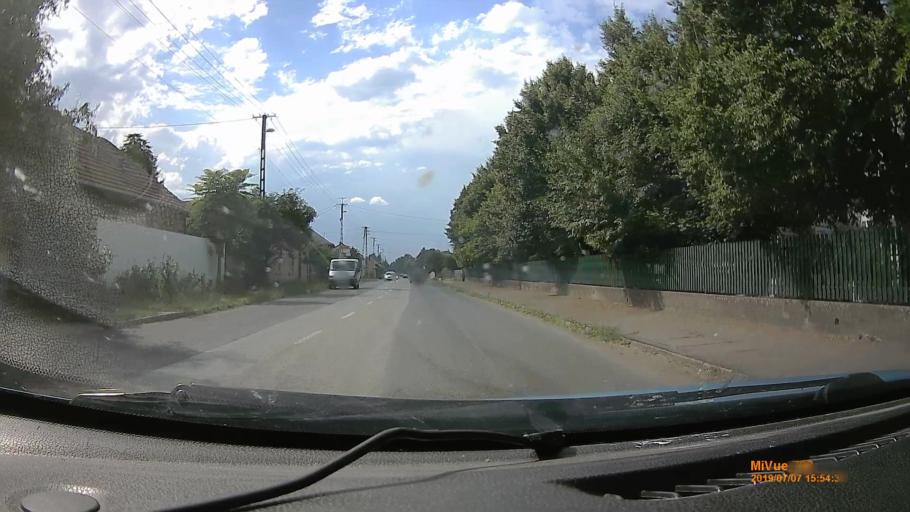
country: HU
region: Pest
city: Szentlorinckata
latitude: 47.5550
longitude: 19.7945
